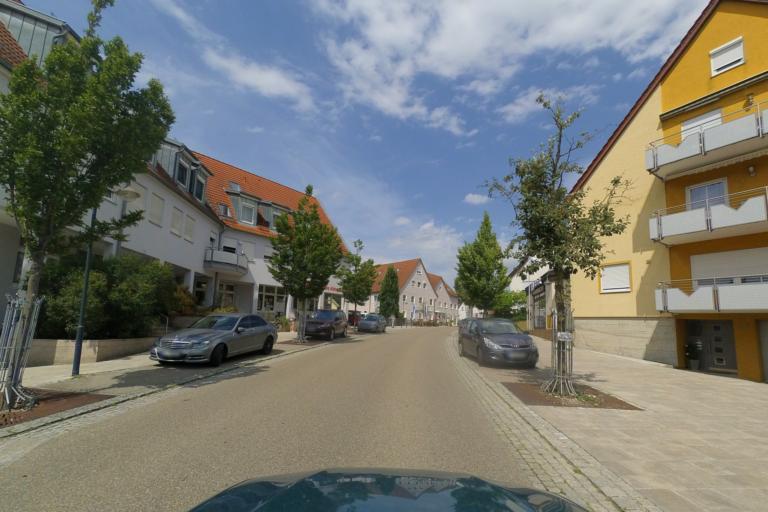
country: DE
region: Baden-Wuerttemberg
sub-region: Regierungsbezirk Stuttgart
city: Abtsgmund
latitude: 48.8935
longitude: 10.0051
